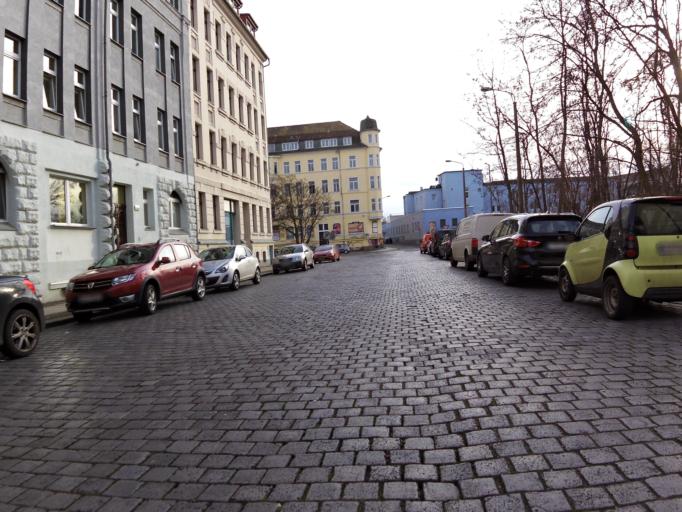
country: DE
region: Saxony
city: Leipzig
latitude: 51.3436
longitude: 12.3970
